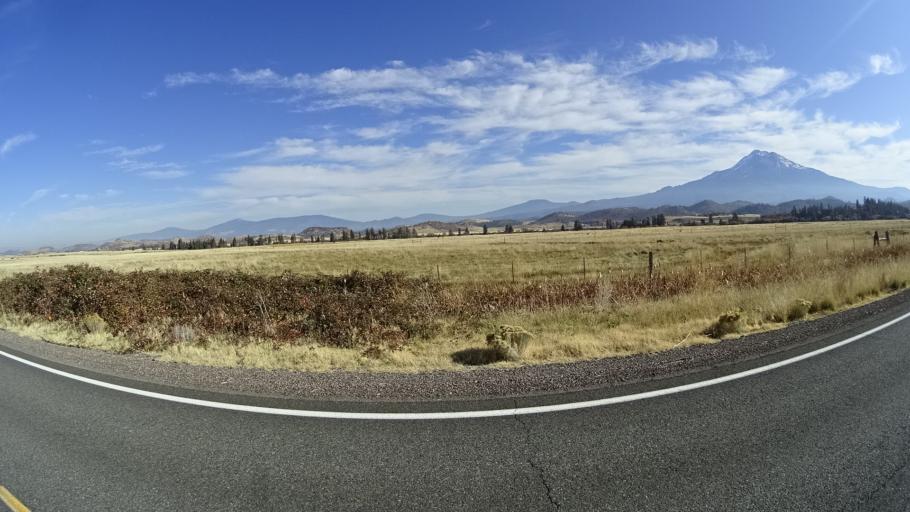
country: US
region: California
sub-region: Siskiyou County
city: Weed
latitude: 41.4552
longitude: -122.4596
